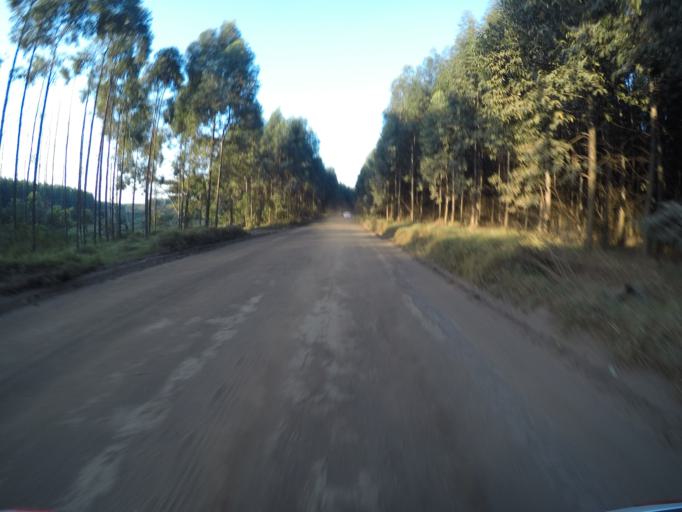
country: ZA
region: KwaZulu-Natal
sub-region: uThungulu District Municipality
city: KwaMbonambi
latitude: -28.6736
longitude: 32.1074
